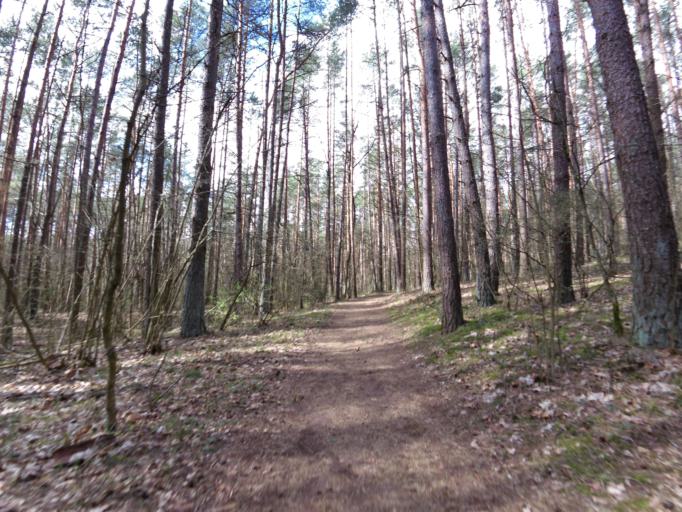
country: LT
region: Vilnius County
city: Pilaite
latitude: 54.6919
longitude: 25.1955
